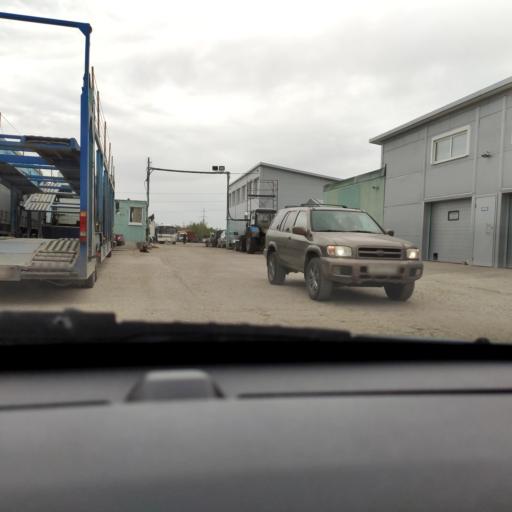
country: RU
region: Samara
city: Tol'yatti
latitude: 53.5460
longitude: 49.2831
